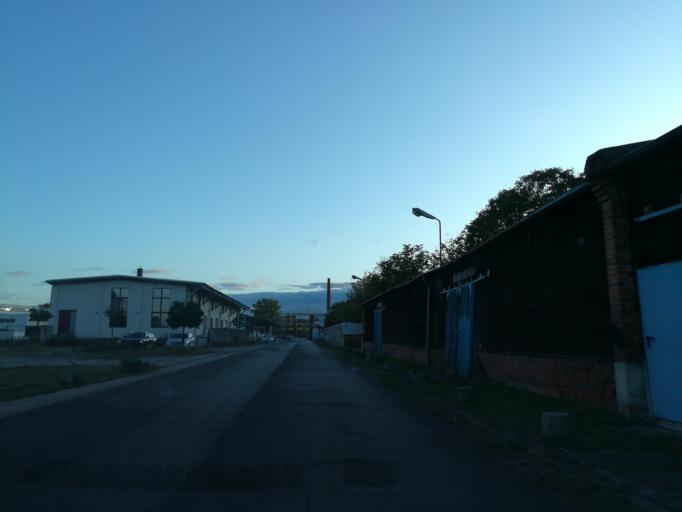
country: DE
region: Saxony-Anhalt
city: Neue Neustadt
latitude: 52.1440
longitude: 11.6569
